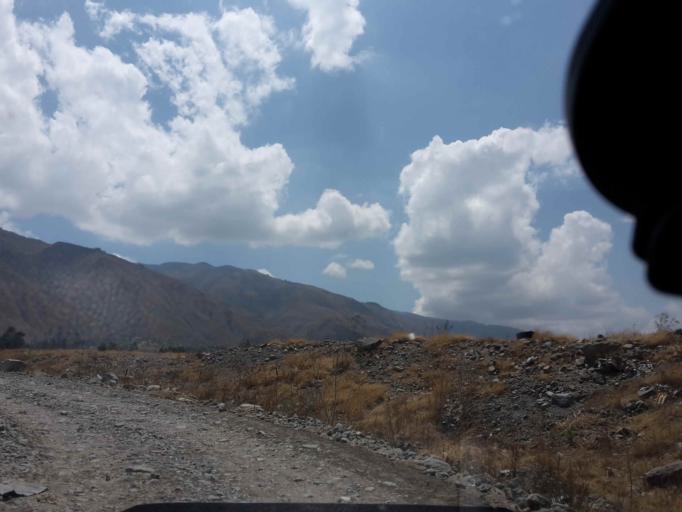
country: BO
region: Cochabamba
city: Cochabamba
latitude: -17.3345
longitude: -66.2118
